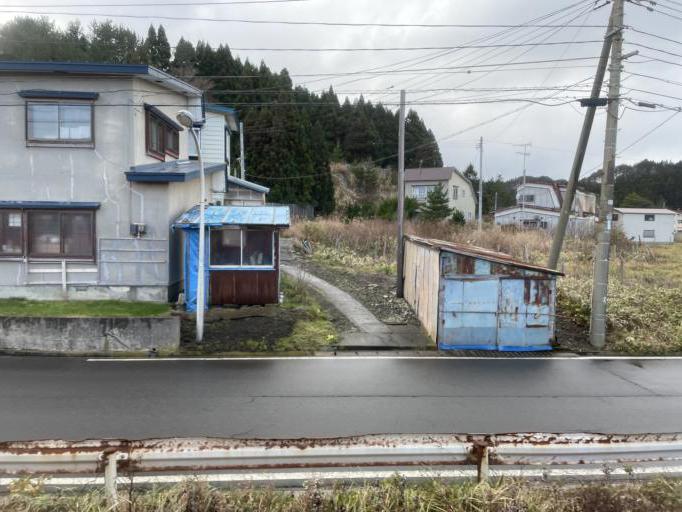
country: JP
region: Aomori
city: Aomori Shi
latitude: 41.0354
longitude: 140.6454
